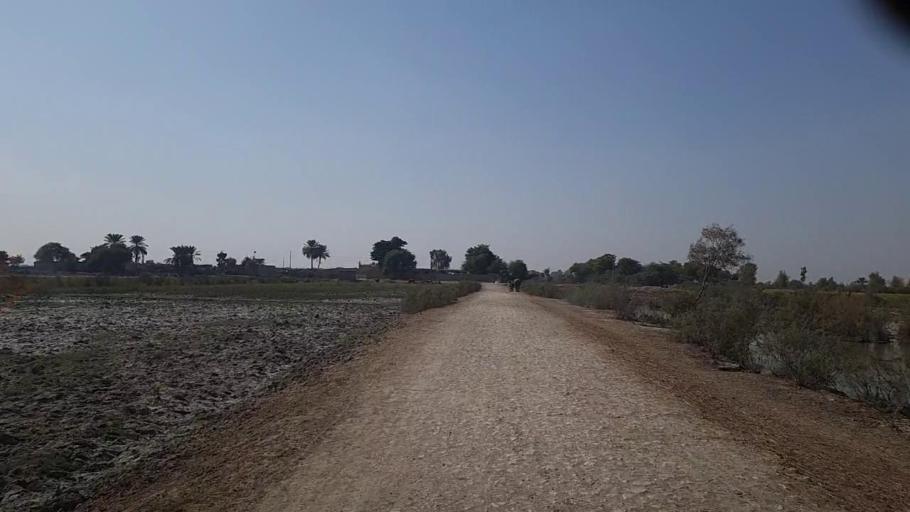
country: PK
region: Sindh
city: Thul
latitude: 28.1733
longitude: 68.7713
